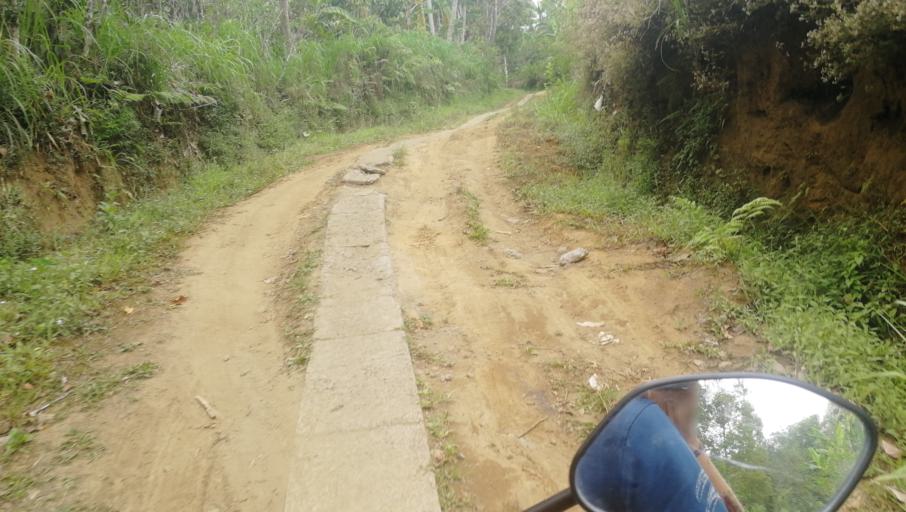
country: ID
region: Bali
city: Munduk
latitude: -8.3085
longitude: 115.0599
